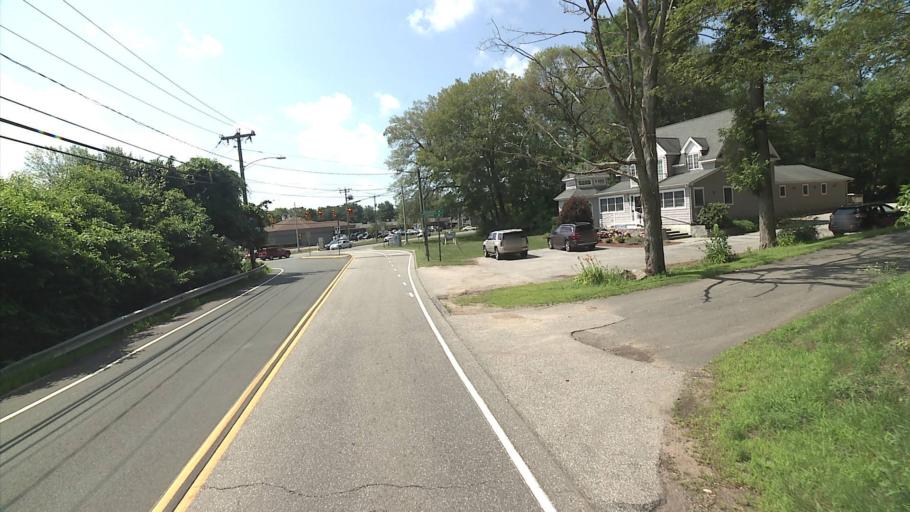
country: US
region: Connecticut
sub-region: Middlesex County
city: Essex Village
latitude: 41.3413
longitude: -72.4144
